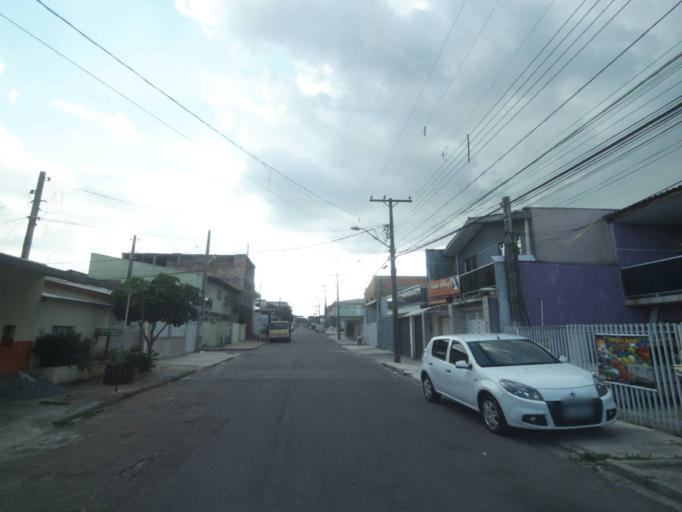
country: BR
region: Parana
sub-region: Sao Jose Dos Pinhais
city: Sao Jose dos Pinhais
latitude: -25.5330
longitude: -49.2754
